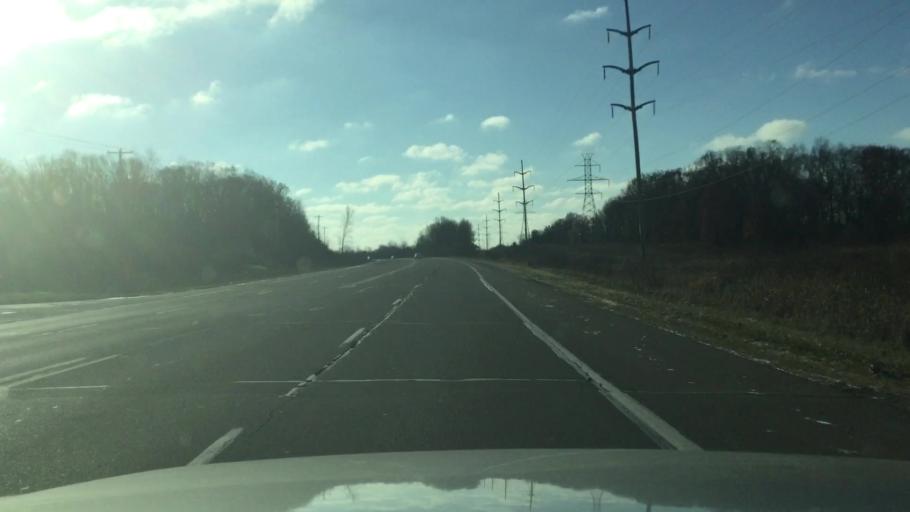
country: US
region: Michigan
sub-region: Genesee County
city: Grand Blanc
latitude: 42.9247
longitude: -83.6510
